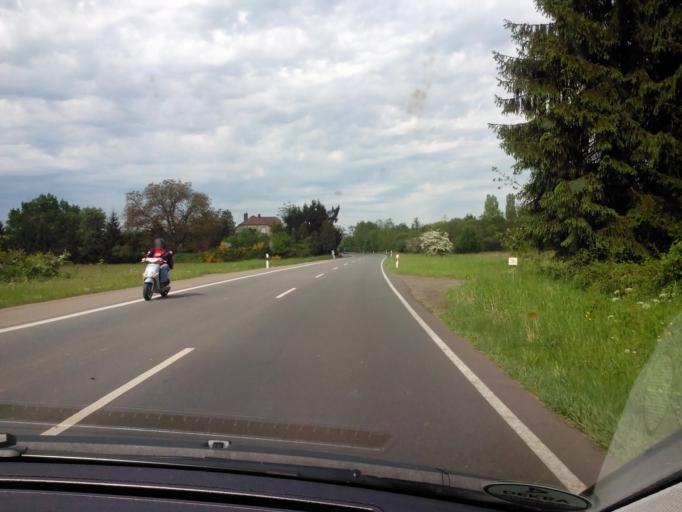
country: DE
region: Saarland
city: Schmelz
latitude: 49.4079
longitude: 6.8480
